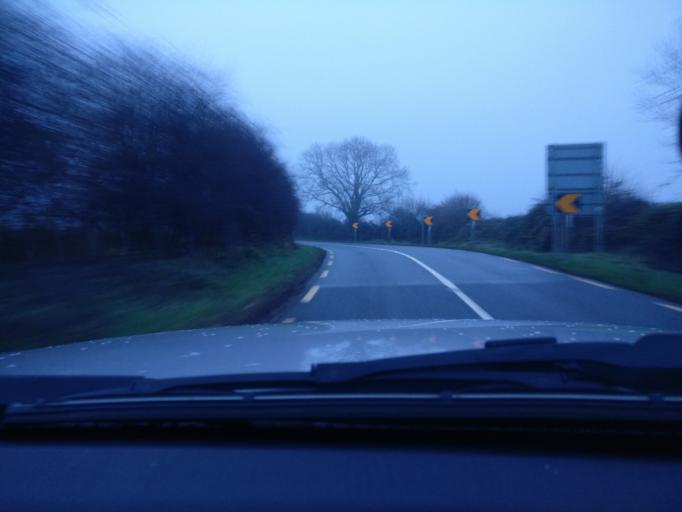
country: IE
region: Leinster
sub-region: An Mhi
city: Athboy
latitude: 53.6066
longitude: -6.9786
